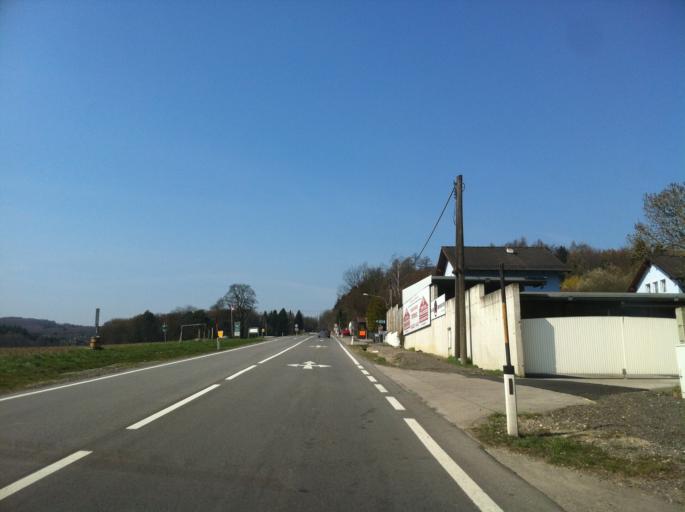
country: AT
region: Lower Austria
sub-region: Politischer Bezirk Wien-Umgebung
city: Gablitz
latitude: 48.2428
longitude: 16.1195
